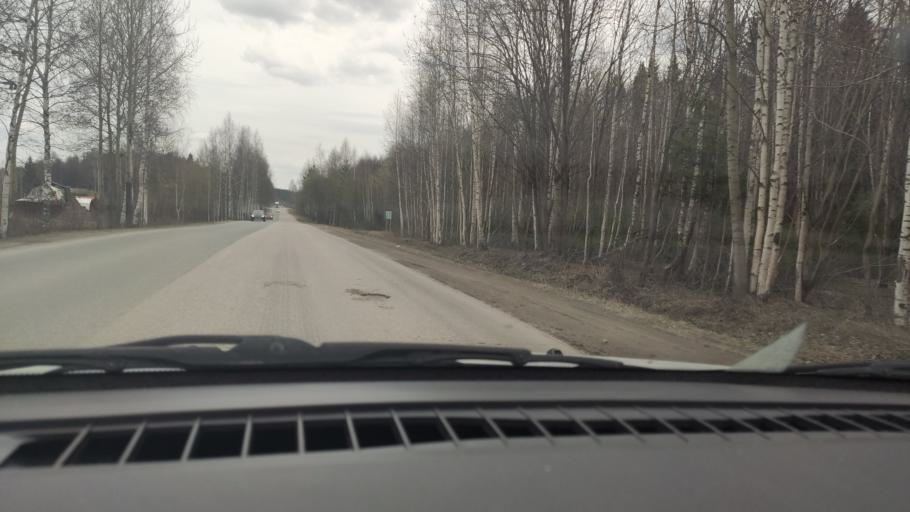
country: RU
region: Perm
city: Perm
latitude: 58.1032
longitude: 56.4141
